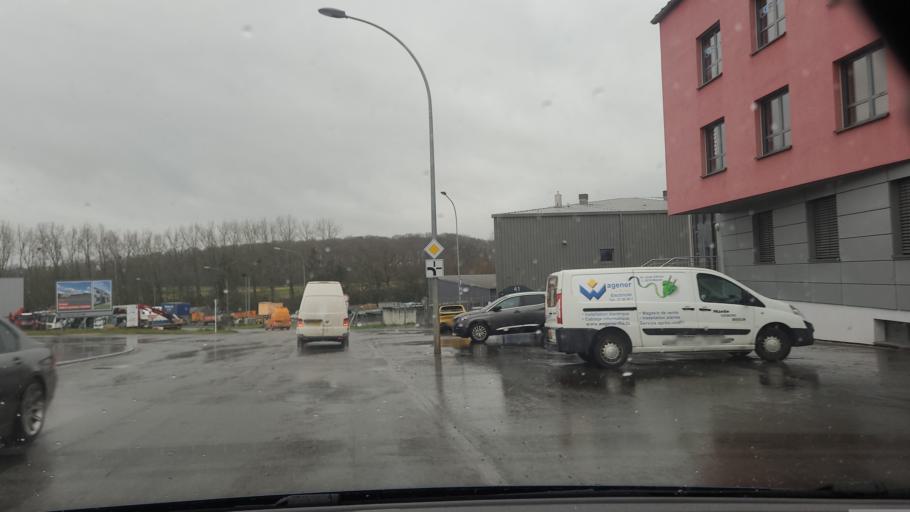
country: LU
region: Luxembourg
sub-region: Canton de Luxembourg
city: Olm
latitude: 49.6630
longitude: 6.0129
